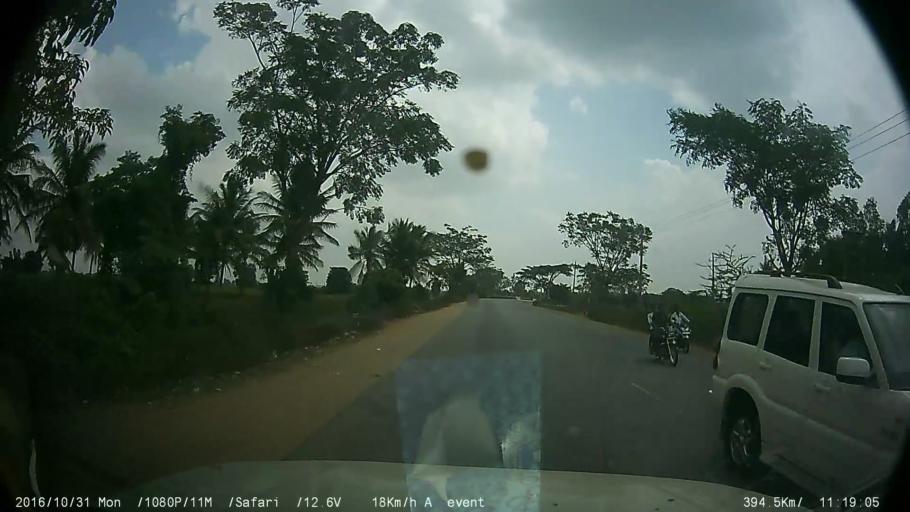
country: IN
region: Karnataka
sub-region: Mysore
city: Piriyapatna
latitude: 12.3389
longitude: 76.1438
